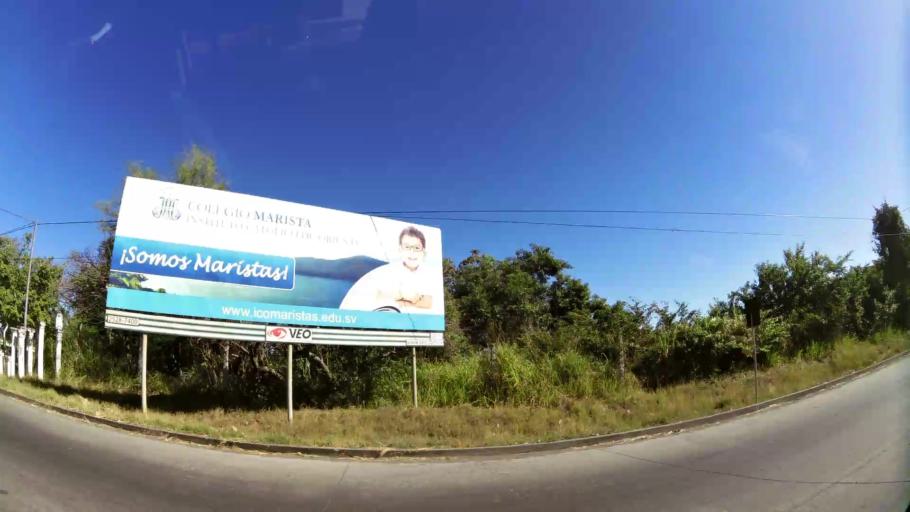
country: SV
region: San Miguel
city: San Miguel
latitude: 13.4593
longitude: -88.1583
